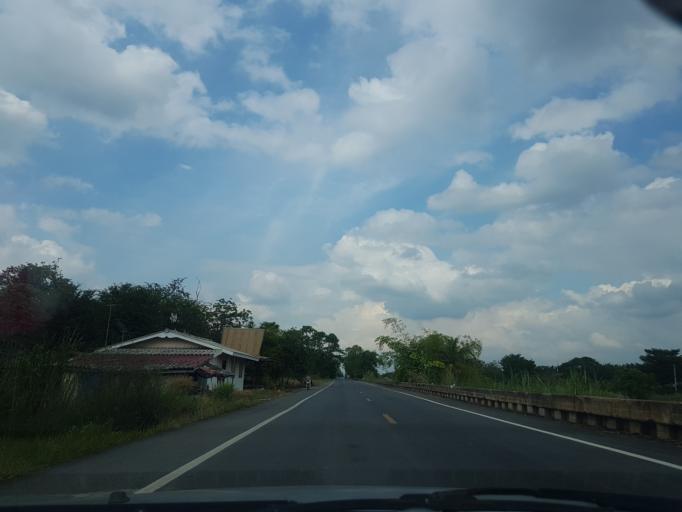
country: TH
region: Pathum Thani
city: Nong Suea
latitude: 14.1905
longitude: 100.8915
